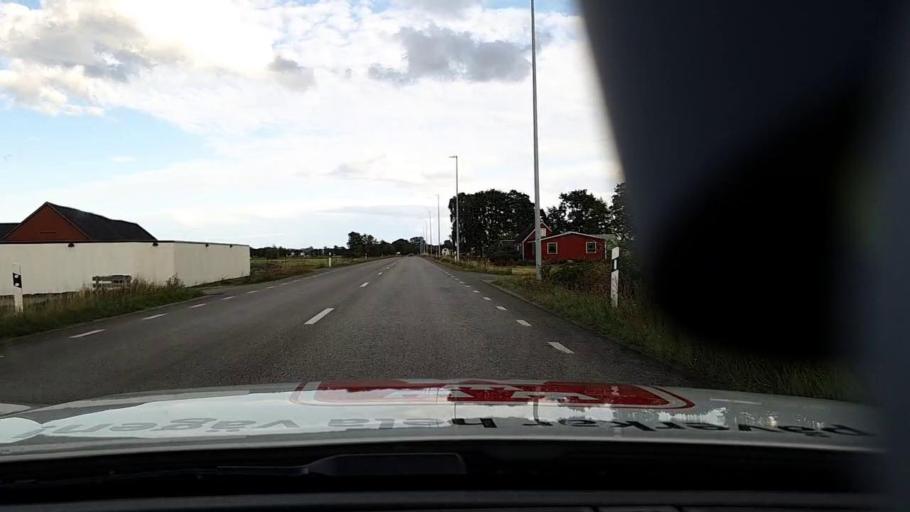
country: SE
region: Blekinge
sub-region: Solvesborgs Kommun
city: Soelvesborg
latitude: 56.0532
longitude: 14.6437
